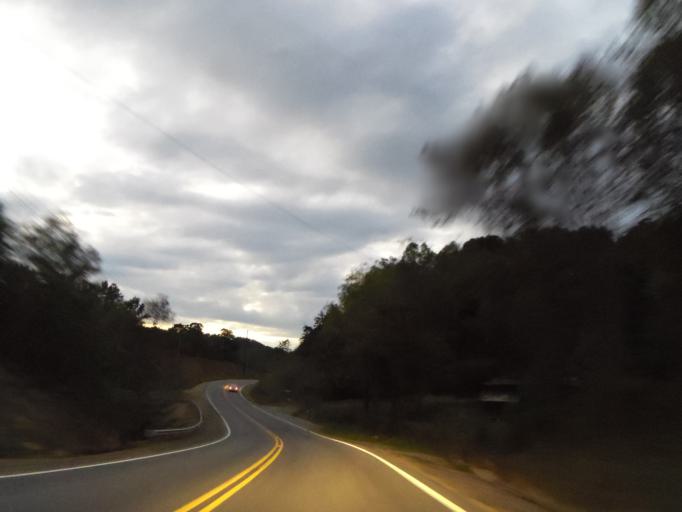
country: US
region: North Carolina
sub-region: Madison County
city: Marshall
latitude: 35.8843
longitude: -82.7401
